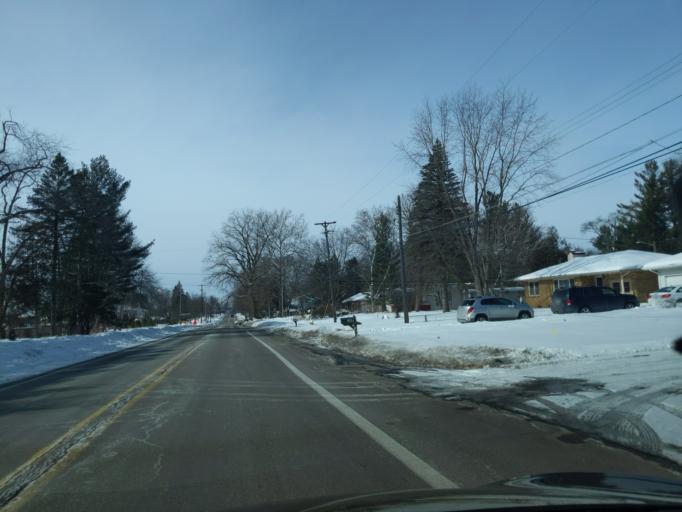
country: US
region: Michigan
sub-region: Kent County
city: Comstock Park
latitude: 43.0134
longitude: -85.6473
